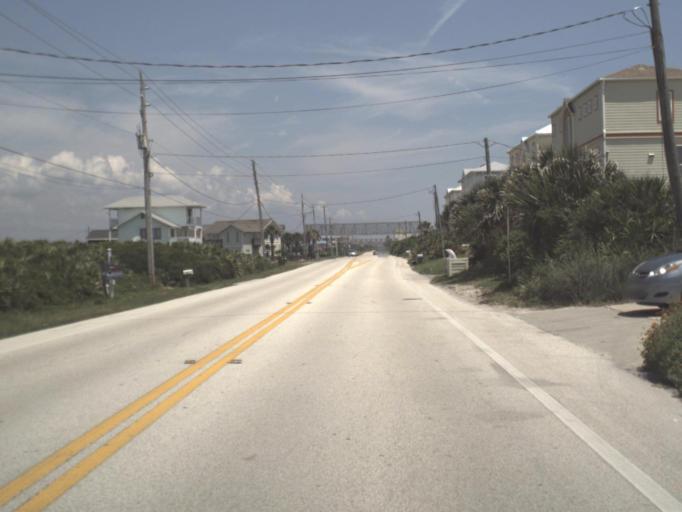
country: US
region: Florida
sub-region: Saint Johns County
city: Villano Beach
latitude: 29.9359
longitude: -81.2989
